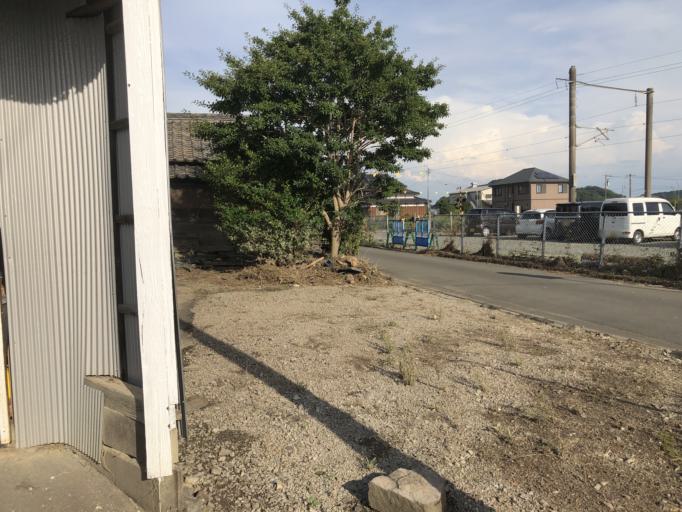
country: JP
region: Saga Prefecture
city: Takeocho-takeo
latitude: 33.2168
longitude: 130.0742
